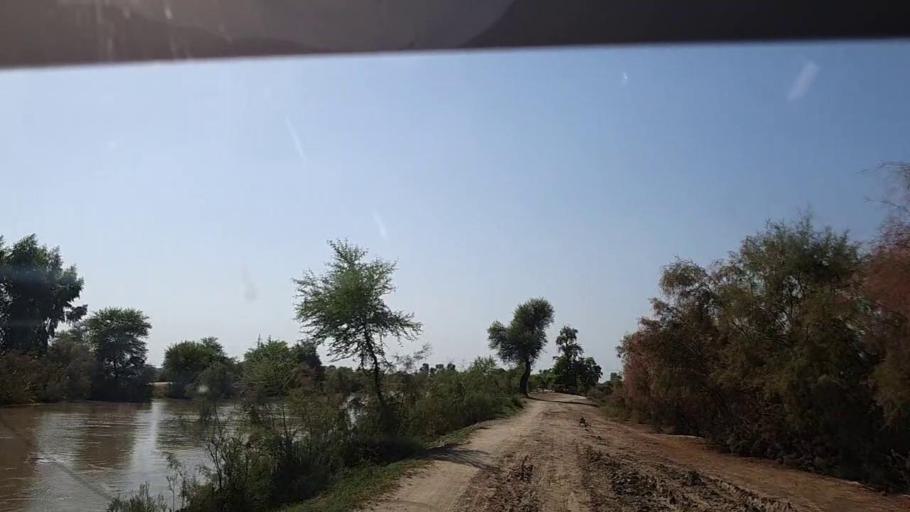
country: PK
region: Sindh
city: Ghauspur
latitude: 28.1835
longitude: 69.0825
